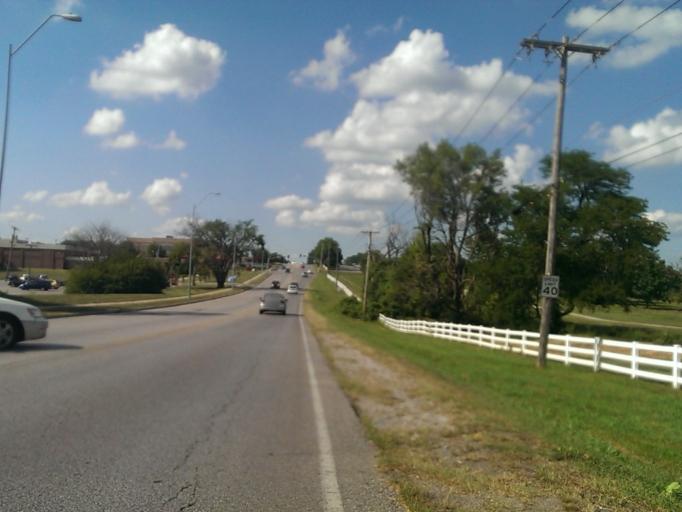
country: US
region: Kansas
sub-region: Johnson County
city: Leawood
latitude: 38.9188
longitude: -94.5838
